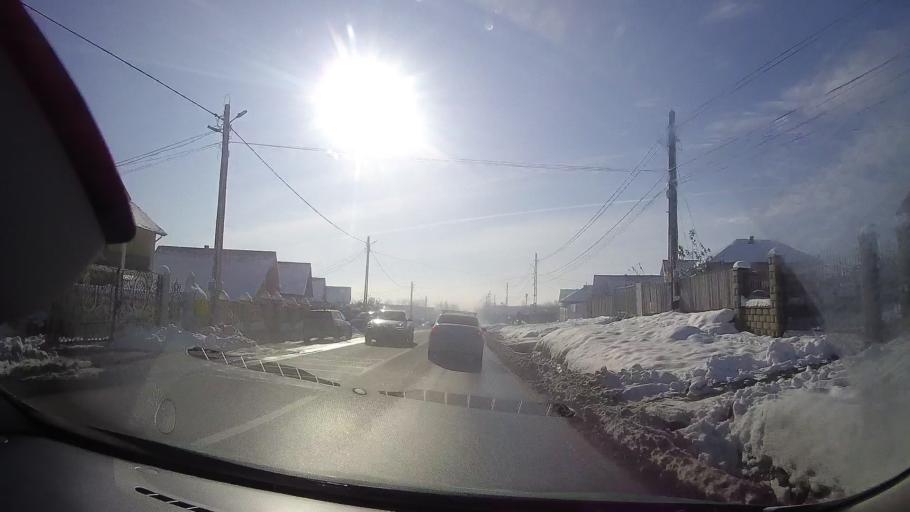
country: RO
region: Iasi
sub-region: Comuna Motca
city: Motca
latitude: 47.2533
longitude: 26.6099
